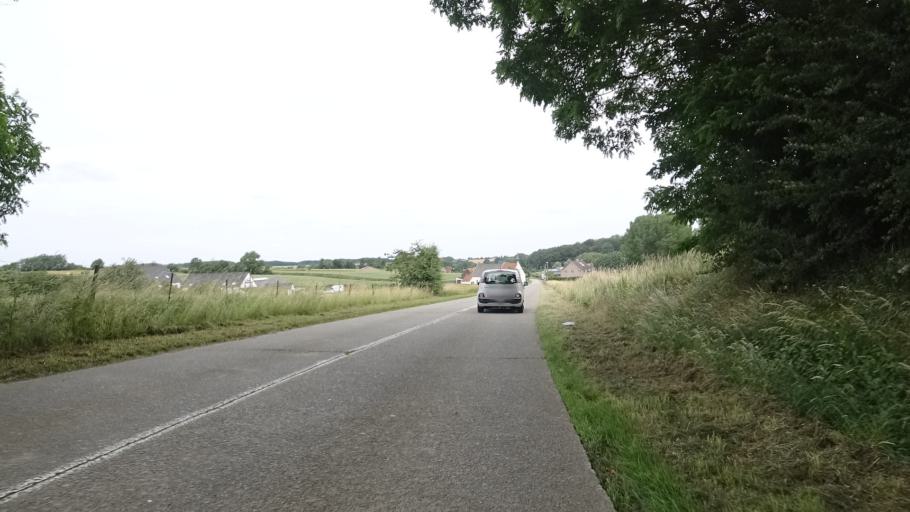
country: BE
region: Wallonia
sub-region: Province du Brabant Wallon
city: Louvain-la-Neuve
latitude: 50.6686
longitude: 4.6514
